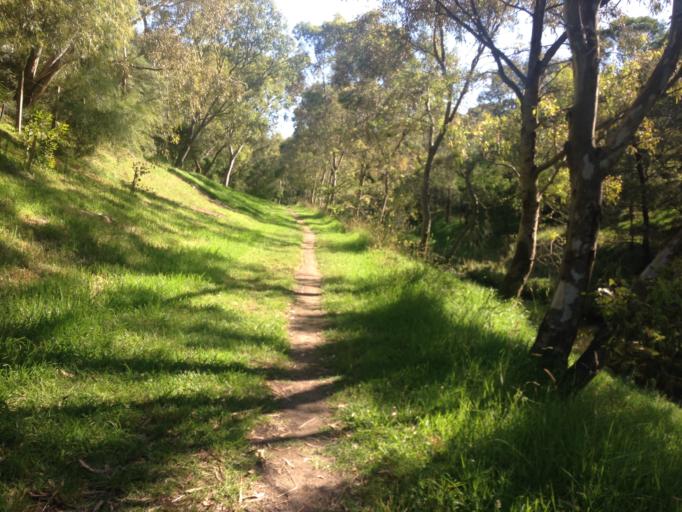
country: AU
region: Victoria
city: Heidelberg West
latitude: -37.7613
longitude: 145.0286
